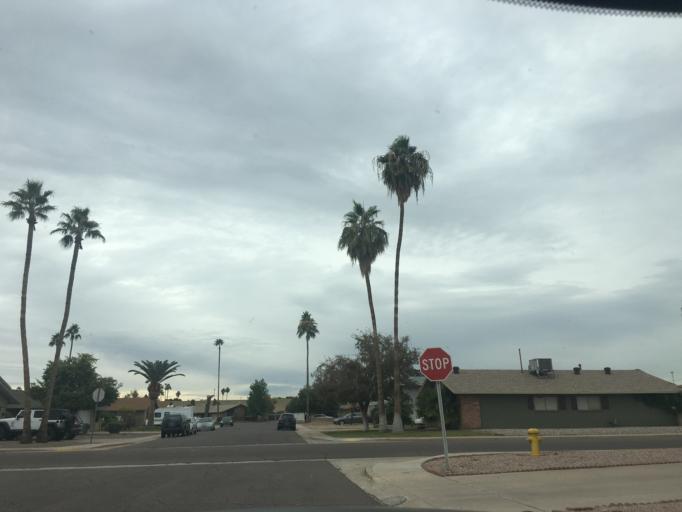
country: US
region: Arizona
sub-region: Maricopa County
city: Tempe
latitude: 33.3836
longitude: -111.9127
